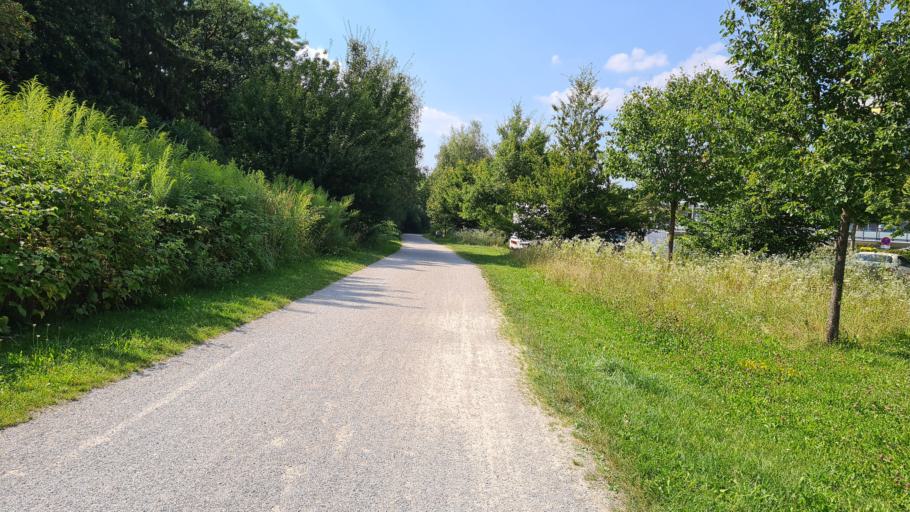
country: DE
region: Bavaria
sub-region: Upper Bavaria
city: Neuried
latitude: 48.1069
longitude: 11.4702
